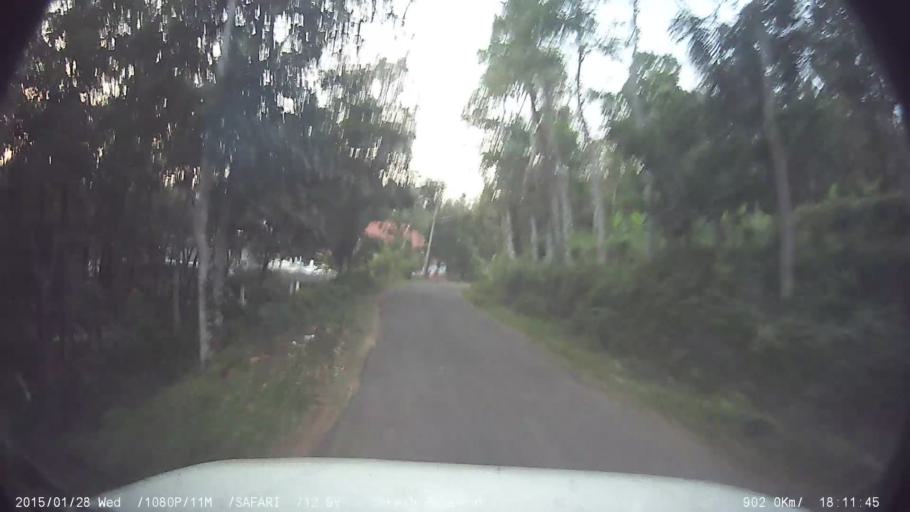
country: IN
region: Kerala
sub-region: Kottayam
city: Palackattumala
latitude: 9.7524
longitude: 76.5679
